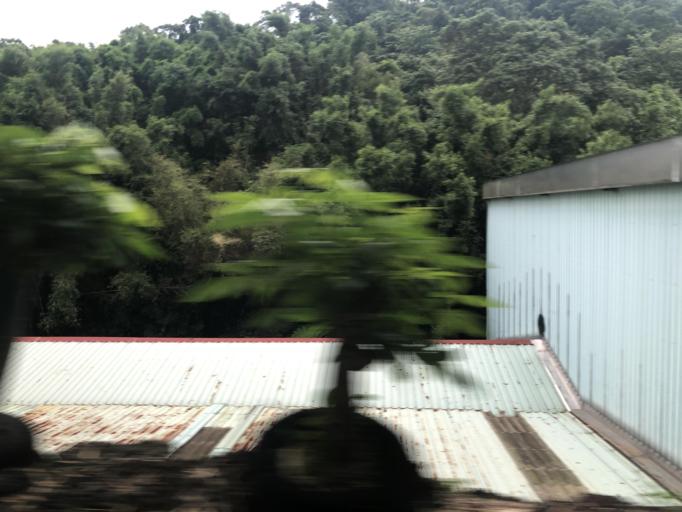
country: TW
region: Taiwan
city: Daxi
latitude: 24.9094
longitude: 121.3376
